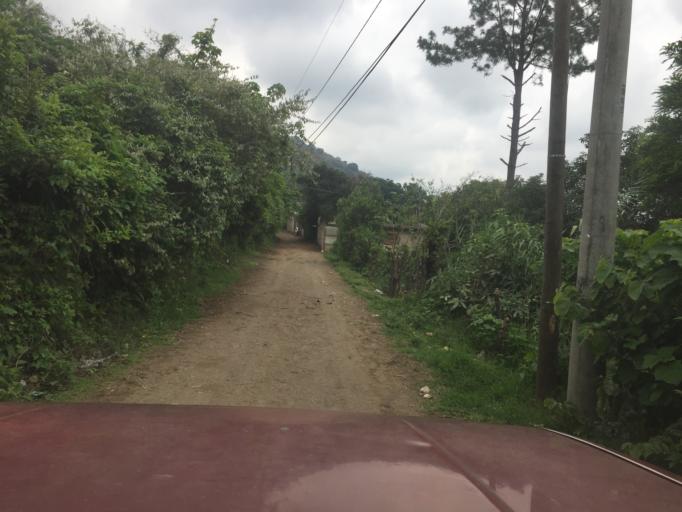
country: GT
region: Sacatepequez
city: Magdalena Milpas Altas
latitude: 14.5094
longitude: -90.6522
